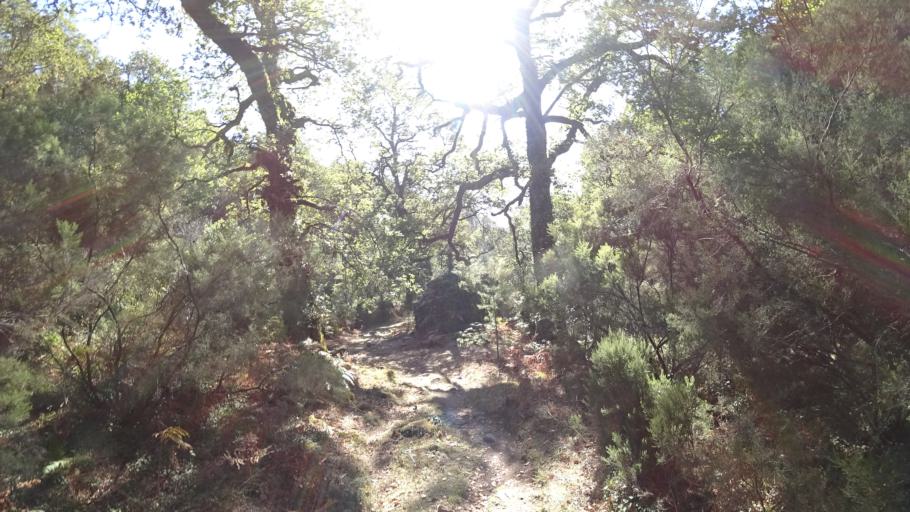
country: PT
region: Braga
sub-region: Vieira do Minho
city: Real
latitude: 41.7582
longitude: -8.1494
